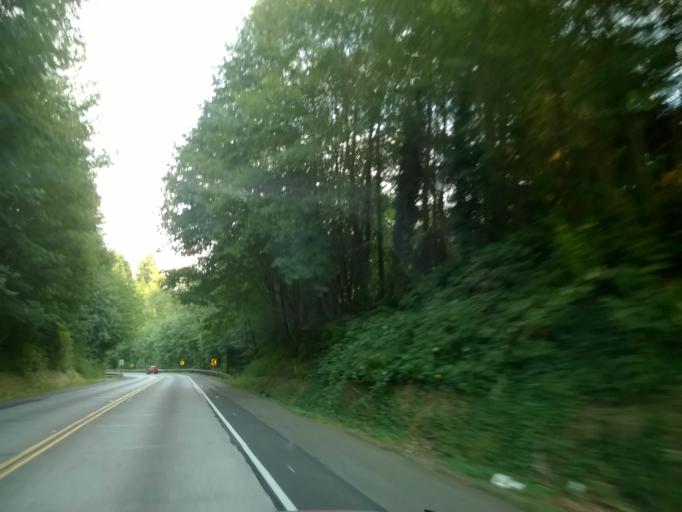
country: US
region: Washington
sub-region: King County
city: Cottage Lake
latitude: 47.7143
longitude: -122.0948
